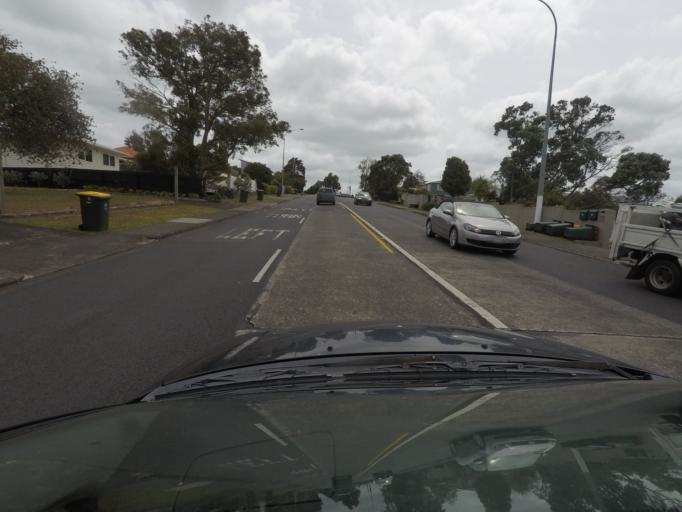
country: NZ
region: Auckland
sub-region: Auckland
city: Pakuranga
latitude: -36.8939
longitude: 174.9236
